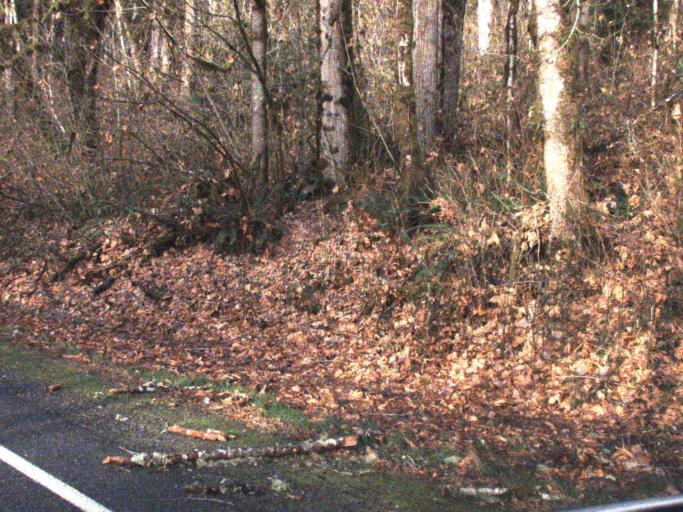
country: US
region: Washington
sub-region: Snohomish County
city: Darrington
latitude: 48.3727
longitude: -121.5424
